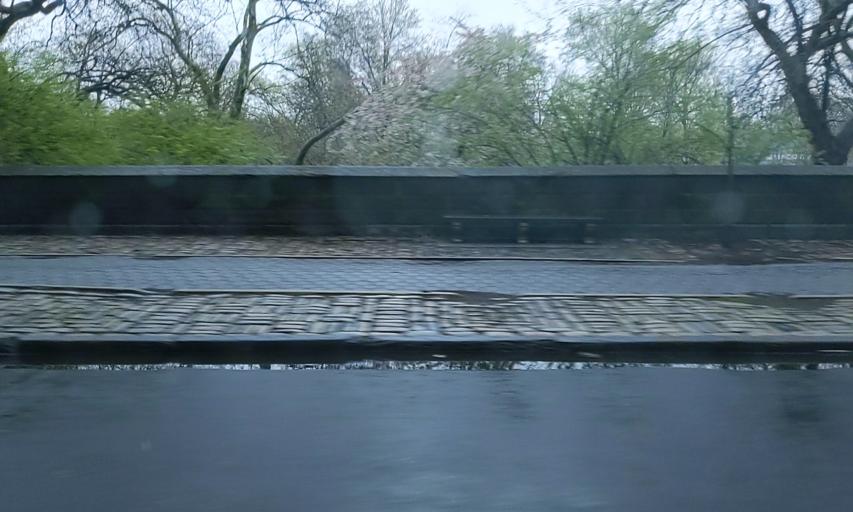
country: US
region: New York
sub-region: New York County
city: Manhattan
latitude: 40.7944
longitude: -73.9627
